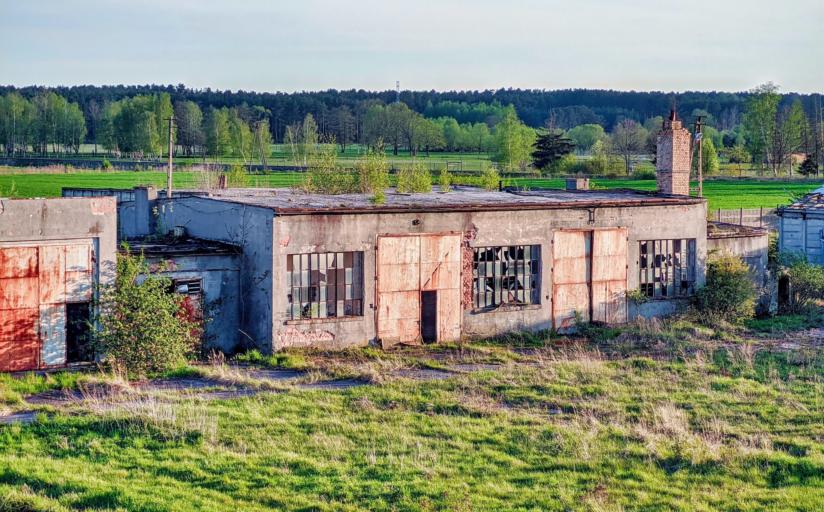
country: PL
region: Lubusz
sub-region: Powiat zaganski
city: Ilowa
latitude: 51.5447
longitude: 15.1962
